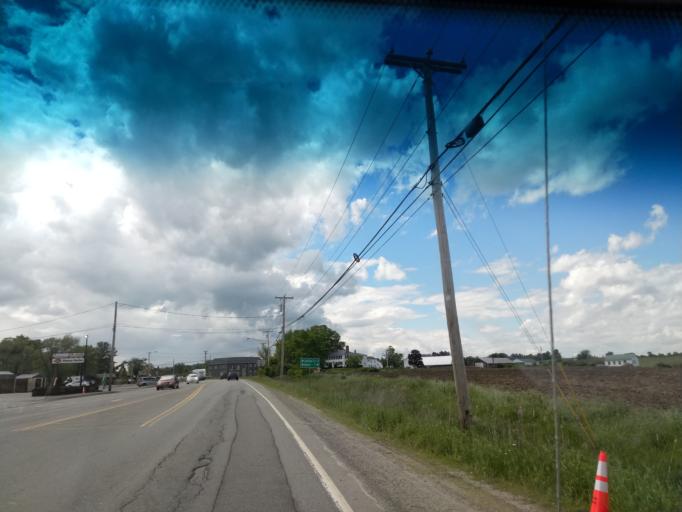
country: US
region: Maine
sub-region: Cumberland County
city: Westbrook
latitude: 43.6902
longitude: -70.3989
